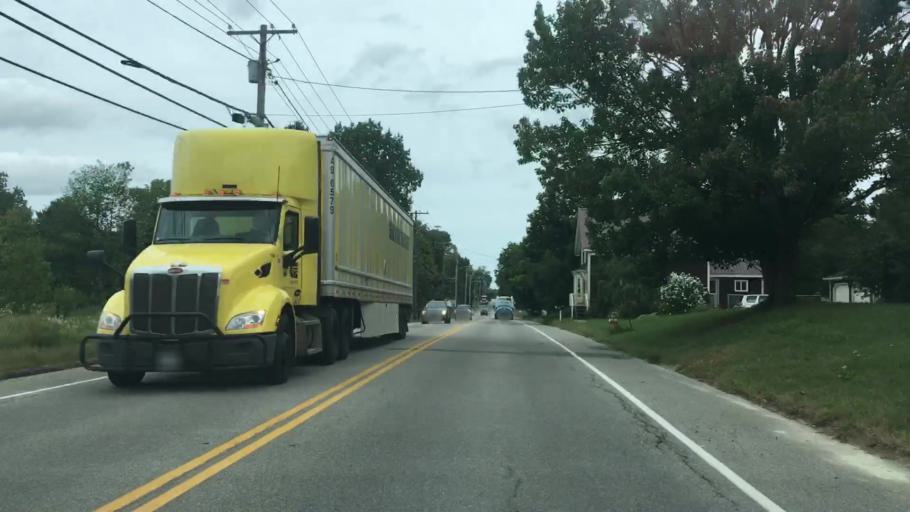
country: US
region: Maine
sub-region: Cumberland County
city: Westbrook
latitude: 43.6672
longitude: -70.3592
